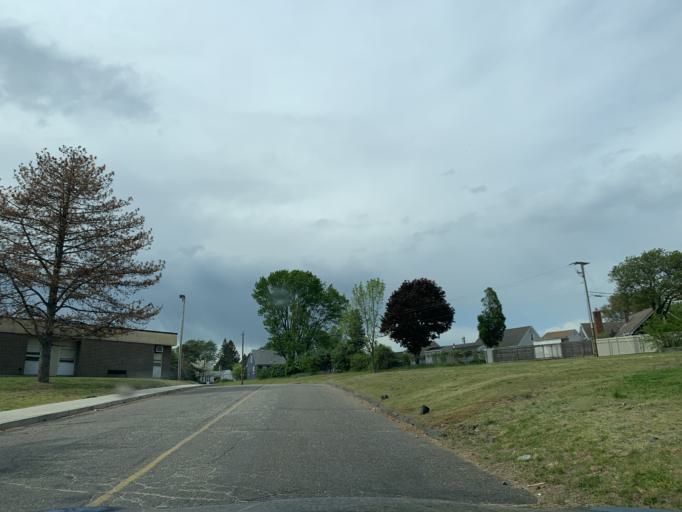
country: US
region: Rhode Island
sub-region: Providence County
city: Cranston
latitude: 41.7748
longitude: -71.4758
